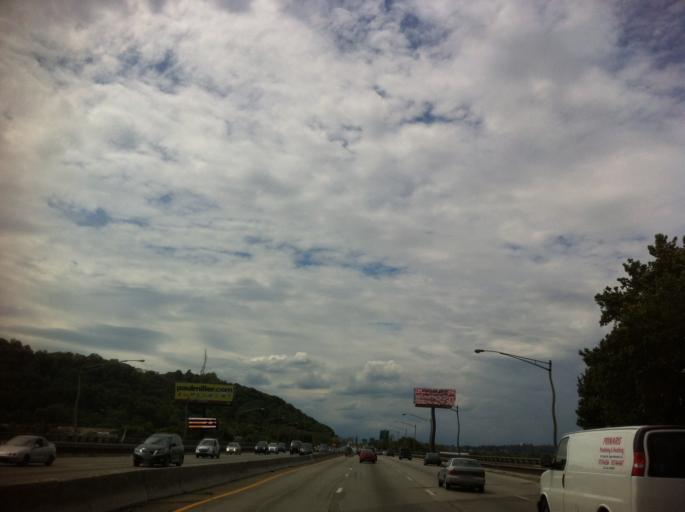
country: US
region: New Jersey
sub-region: Bergen County
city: Elmwood Park
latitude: 40.9007
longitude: -74.1429
